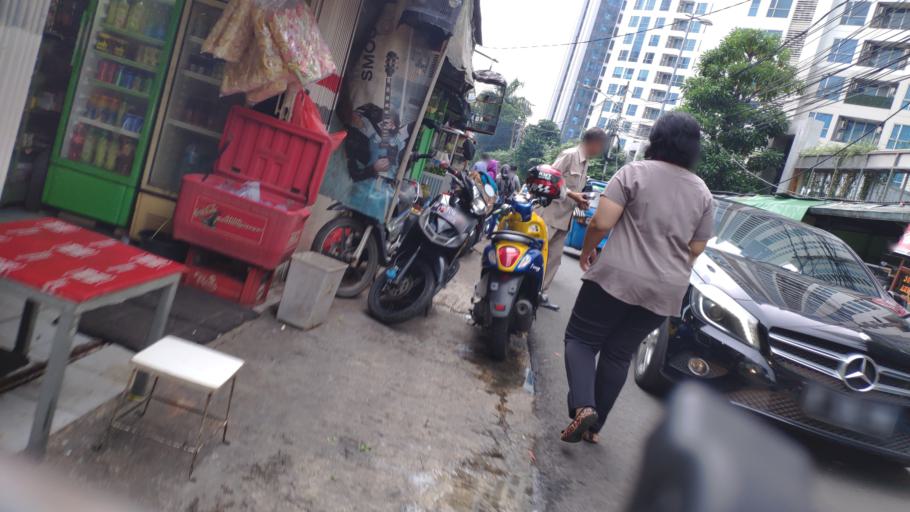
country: ID
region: Jakarta Raya
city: Jakarta
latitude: -6.2244
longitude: 106.8414
